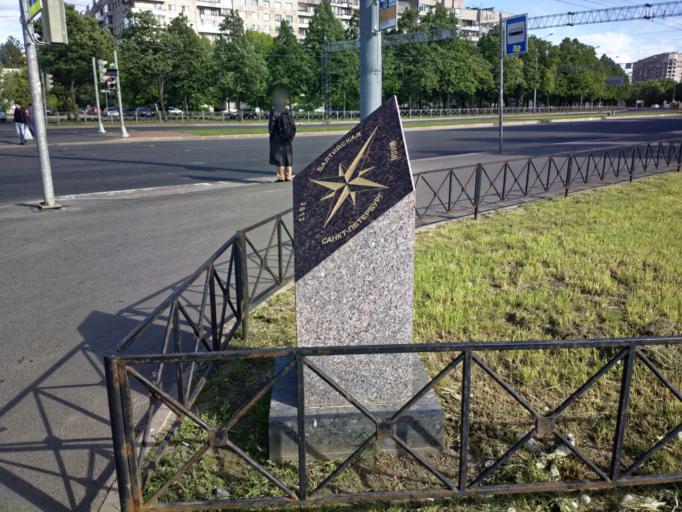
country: RU
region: St.-Petersburg
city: Vasyl'evsky Ostrov
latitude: 59.9459
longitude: 30.2136
